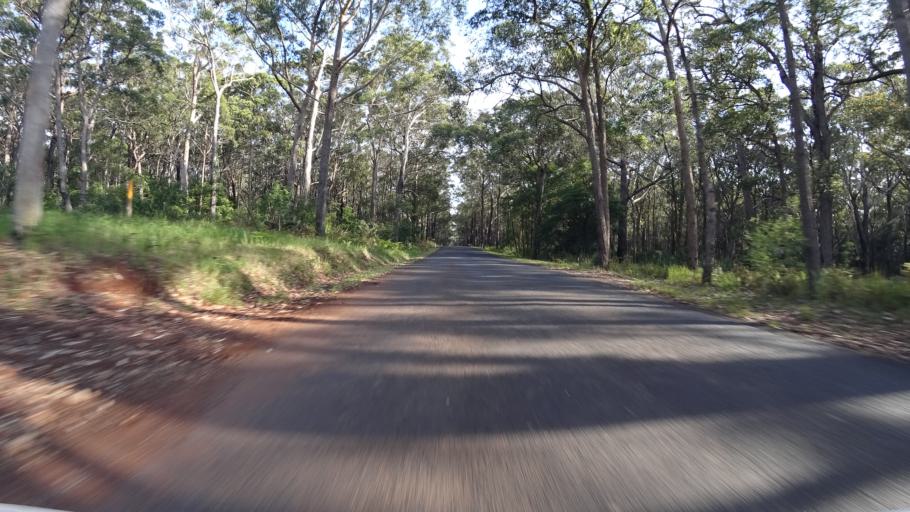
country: AU
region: New South Wales
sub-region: Shoalhaven Shire
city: Milton
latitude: -35.2570
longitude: 150.5054
